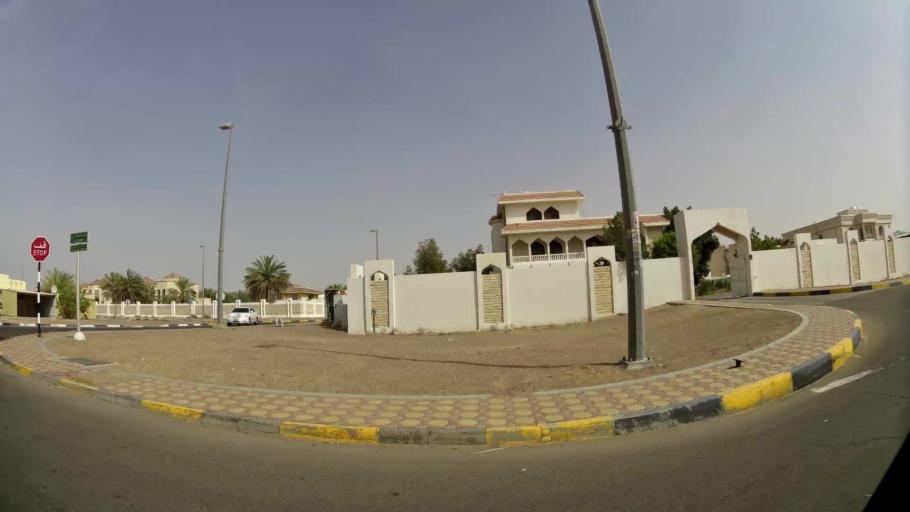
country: AE
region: Abu Dhabi
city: Al Ain
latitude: 24.1808
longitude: 55.6175
